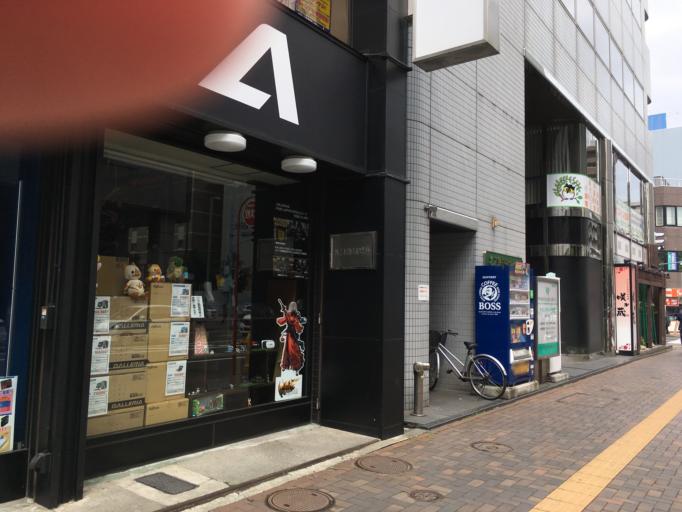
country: JP
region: Hokkaido
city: Sapporo
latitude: 43.0696
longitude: 141.3481
